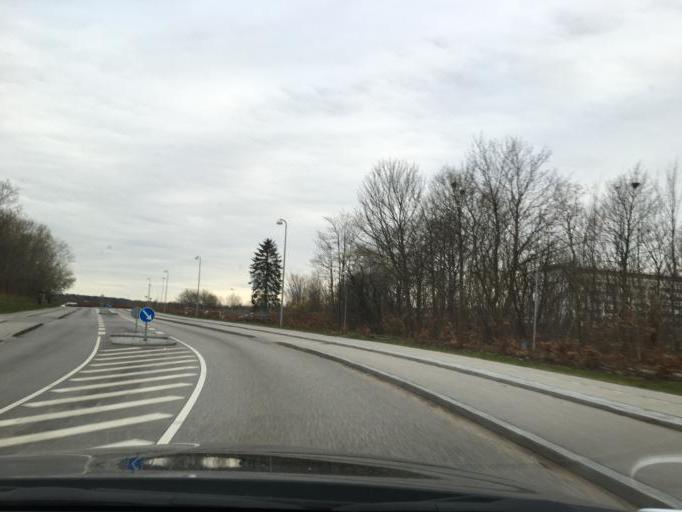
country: DK
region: Capital Region
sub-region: Fredensborg Kommune
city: Kokkedal
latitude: 55.9032
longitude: 12.5037
